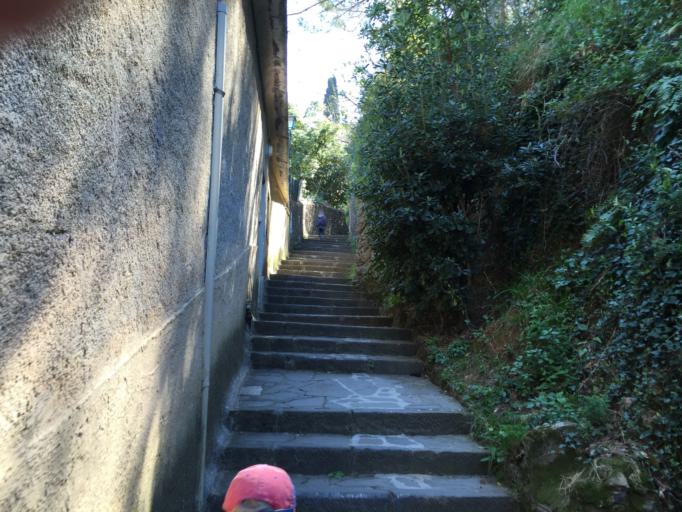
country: IT
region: Liguria
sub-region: Provincia di Genova
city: Portofino
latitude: 44.3016
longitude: 9.2126
